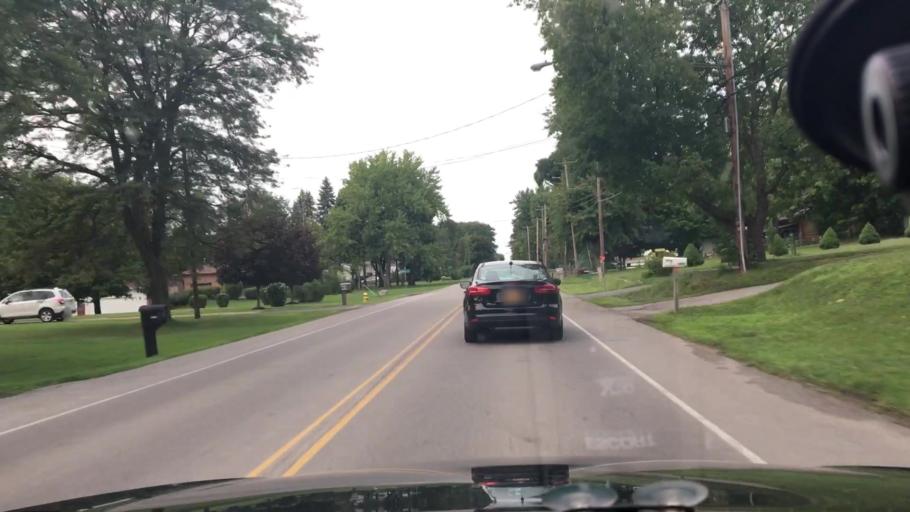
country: US
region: New York
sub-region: Erie County
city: Hamburg
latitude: 42.7473
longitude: -78.7971
